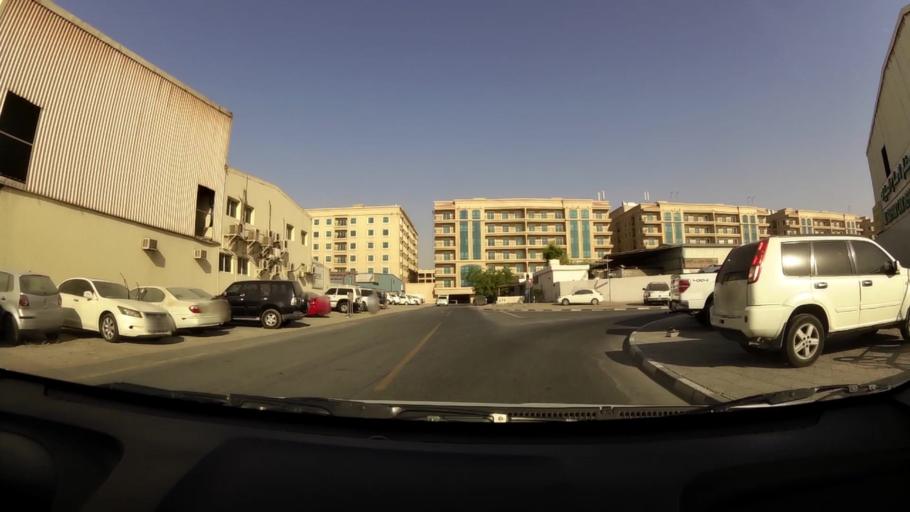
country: AE
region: Ash Shariqah
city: Sharjah
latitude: 25.2883
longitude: 55.3898
